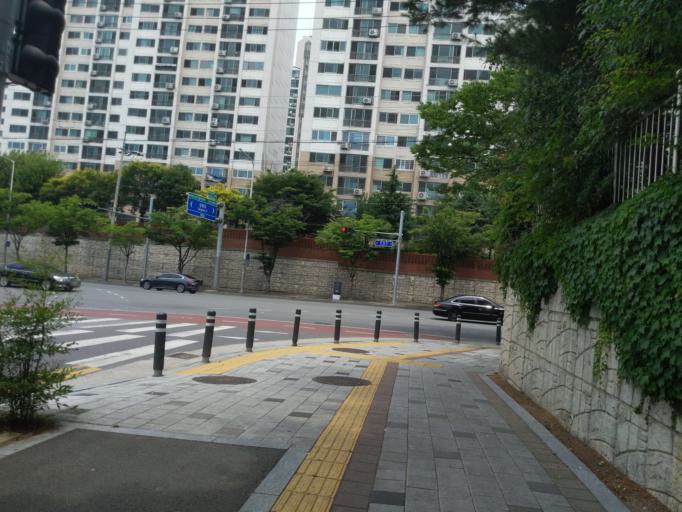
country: KR
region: Daegu
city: Hwawon
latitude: 35.8073
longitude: 128.5285
